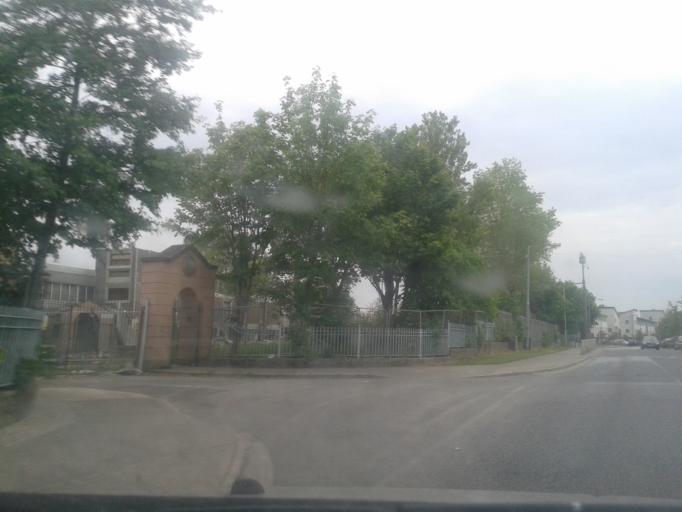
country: IE
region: Leinster
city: Ballymun
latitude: 53.3980
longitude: -6.2690
